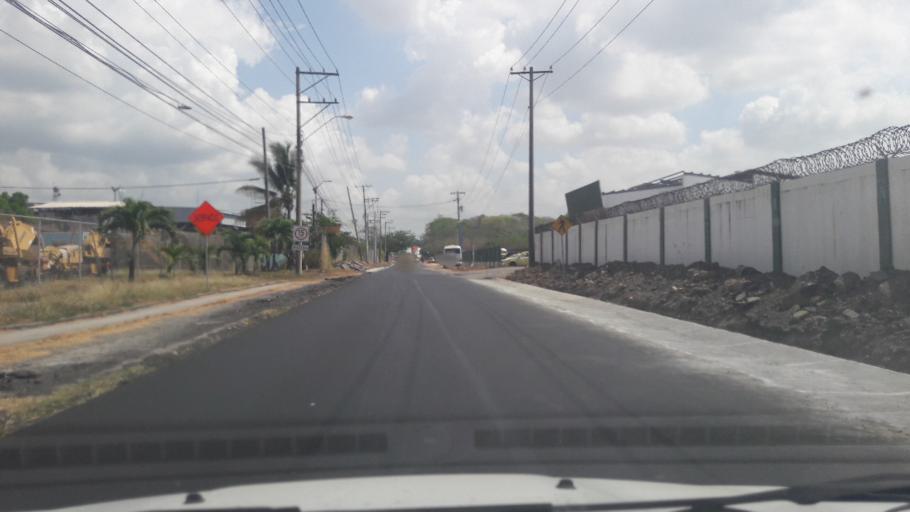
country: PA
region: Panama
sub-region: Distrito de Panama
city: Ancon
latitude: 8.9698
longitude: -79.5473
